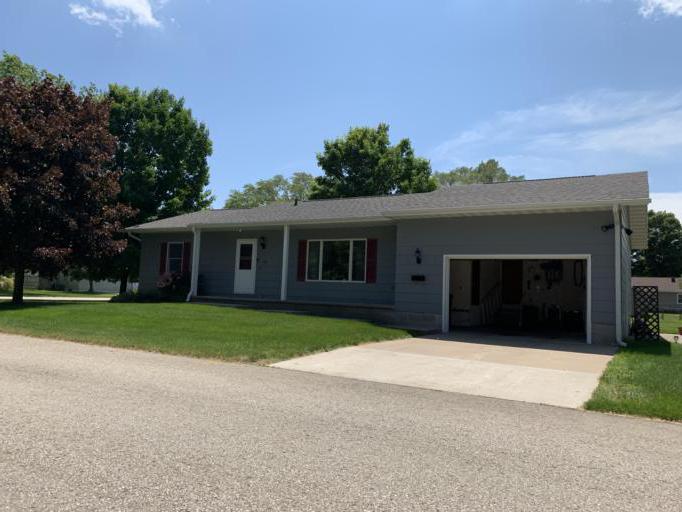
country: US
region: Michigan
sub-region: Menominee County
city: Menominee
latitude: 45.1393
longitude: -87.6039
